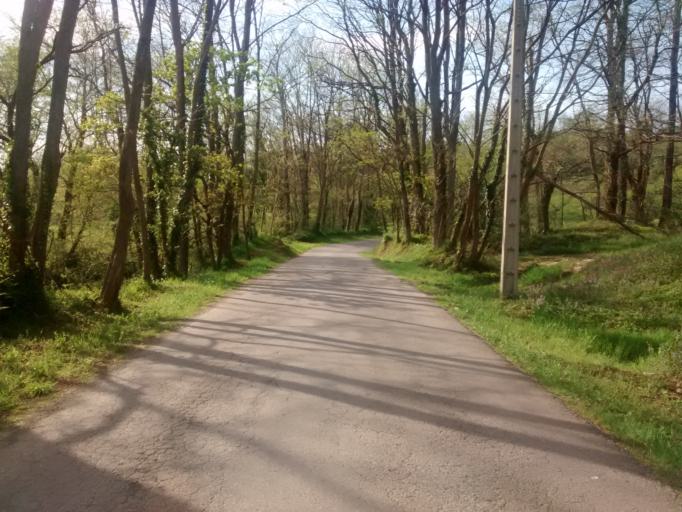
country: ES
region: Cantabria
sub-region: Provincia de Cantabria
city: Entrambasaguas
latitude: 43.3377
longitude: -3.6605
